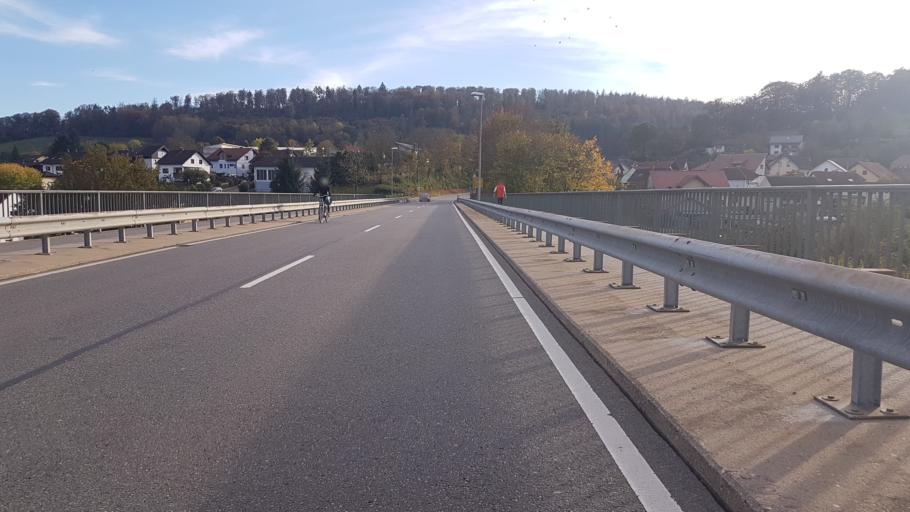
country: DE
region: Baden-Wuerttemberg
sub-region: Karlsruhe Region
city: Neckargerach
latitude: 49.3937
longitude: 9.0703
